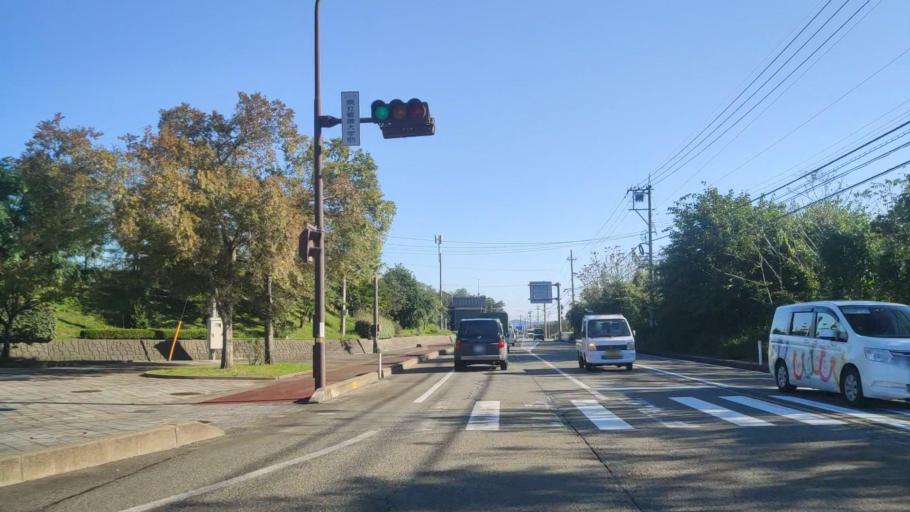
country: JP
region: Ishikawa
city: Tsubata
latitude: 36.7792
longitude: 136.7349
